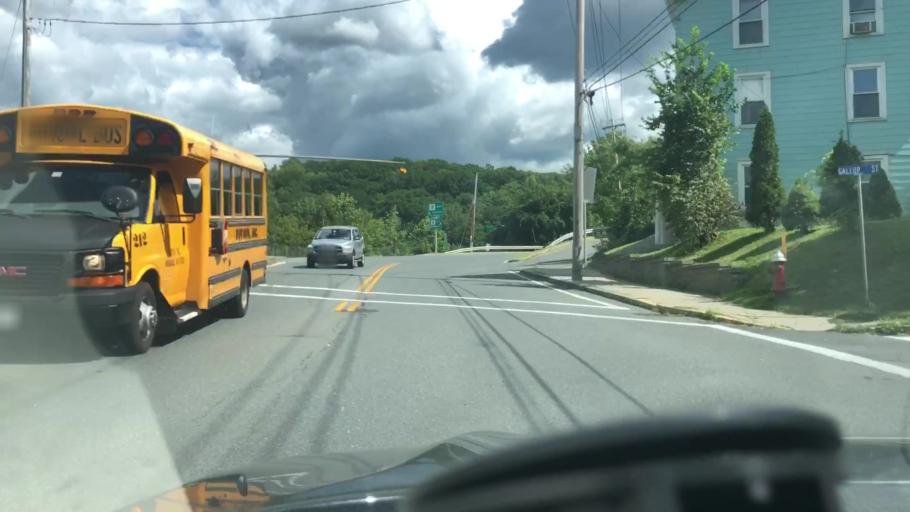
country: US
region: Massachusetts
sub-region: Berkshire County
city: North Adams
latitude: 42.7022
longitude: -73.0968
